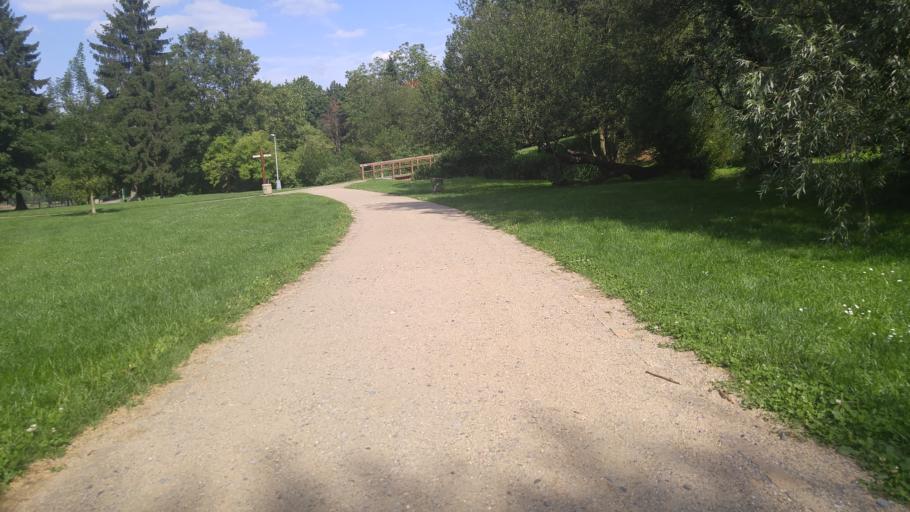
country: CZ
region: Praha
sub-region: Praha 1
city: Mala Strana
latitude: 50.0847
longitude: 14.3601
